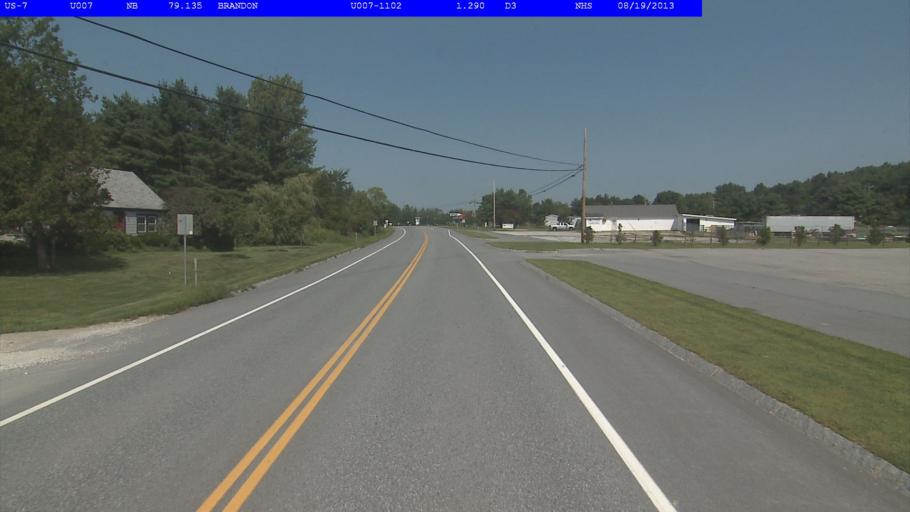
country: US
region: Vermont
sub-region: Rutland County
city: Brandon
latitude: 43.7727
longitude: -73.0523
